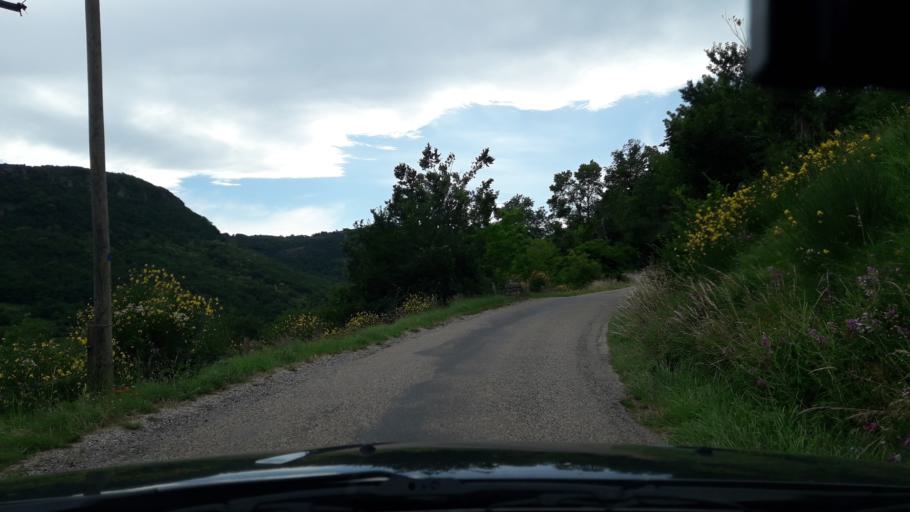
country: FR
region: Rhone-Alpes
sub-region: Departement de l'Ardeche
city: Alissas
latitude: 44.6755
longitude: 4.6198
